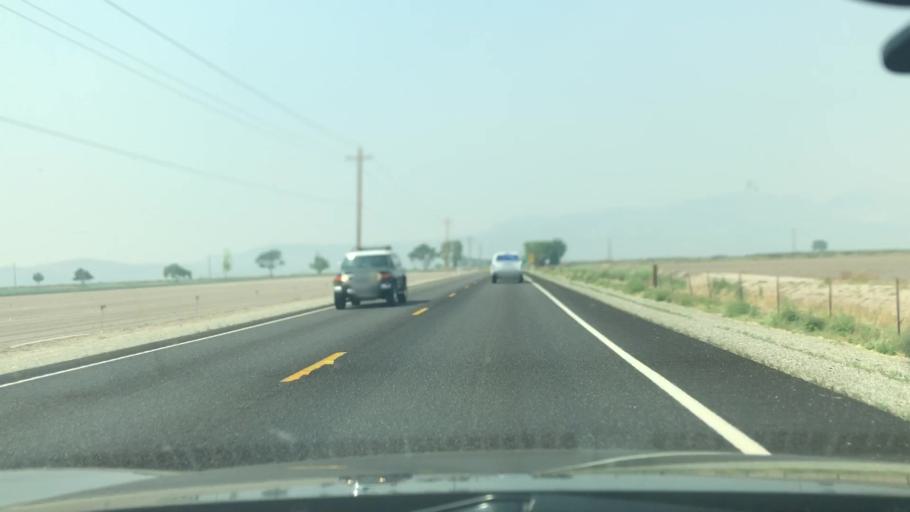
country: US
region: Nevada
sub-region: Lyon County
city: Yerington
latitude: 39.1250
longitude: -119.1810
